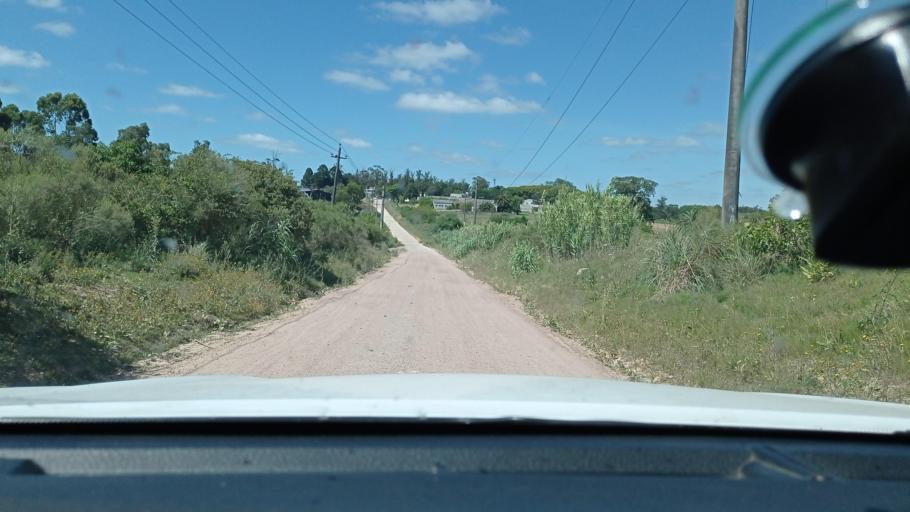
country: UY
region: Canelones
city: Pando
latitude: -34.7287
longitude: -55.9745
